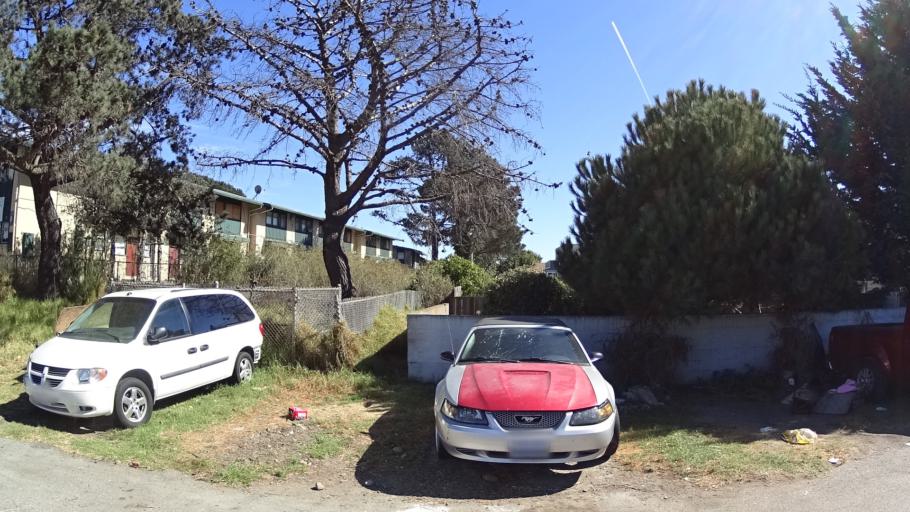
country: US
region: California
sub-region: San Mateo County
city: Brisbane
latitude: 37.7196
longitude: -122.3898
